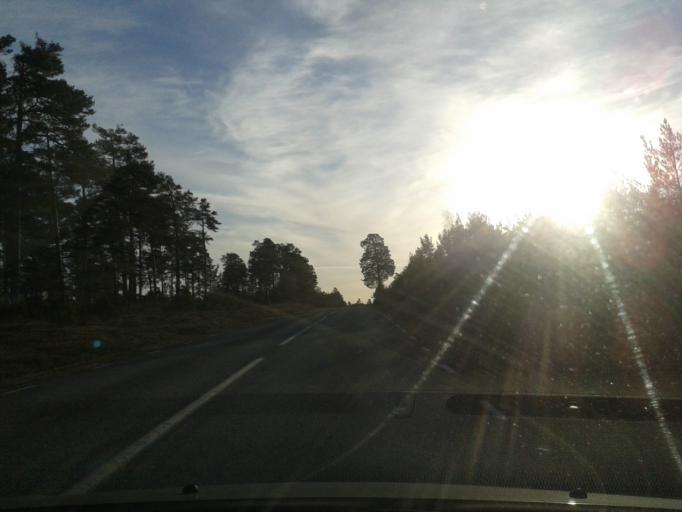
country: SE
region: Gotland
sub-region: Gotland
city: Hemse
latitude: 57.4057
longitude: 18.6367
